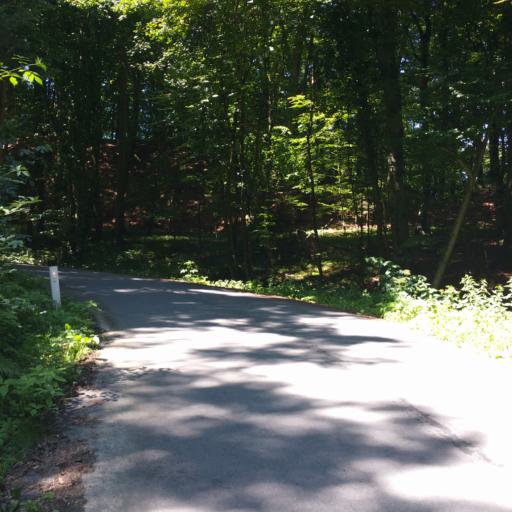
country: AT
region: Styria
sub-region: Politischer Bezirk Leibnitz
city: Gleinstatten
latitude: 46.7366
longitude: 15.3497
